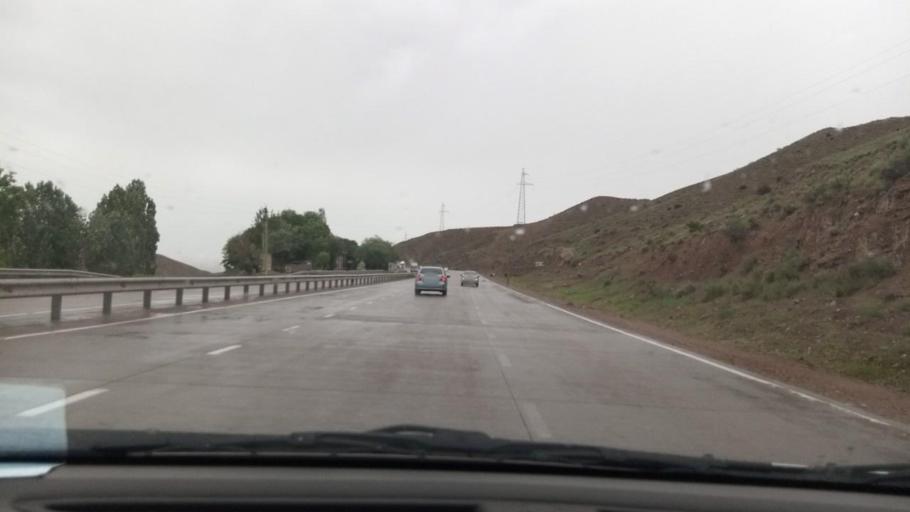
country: UZ
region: Namangan
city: Pop Shahri
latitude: 40.9485
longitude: 70.6807
